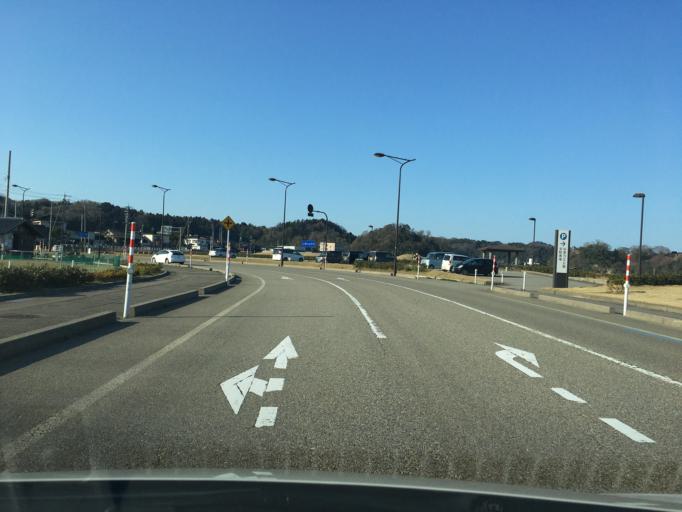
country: JP
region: Toyama
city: Himi
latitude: 36.8734
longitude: 136.9847
